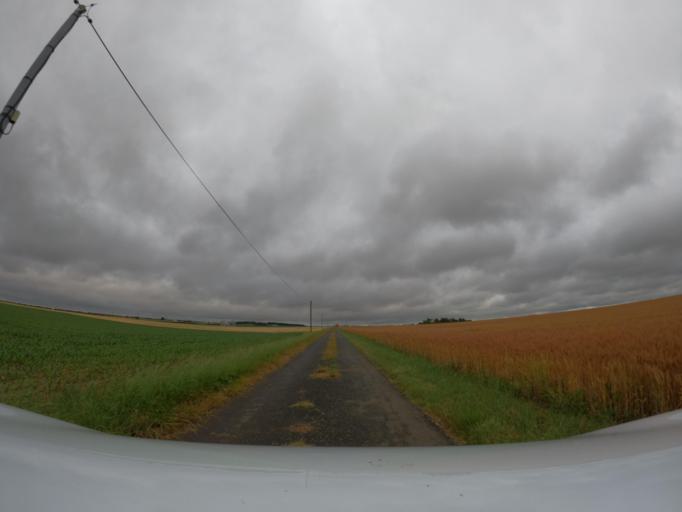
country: FR
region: Pays de la Loire
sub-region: Departement de la Vendee
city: Maillezais
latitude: 46.4072
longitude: -0.7372
